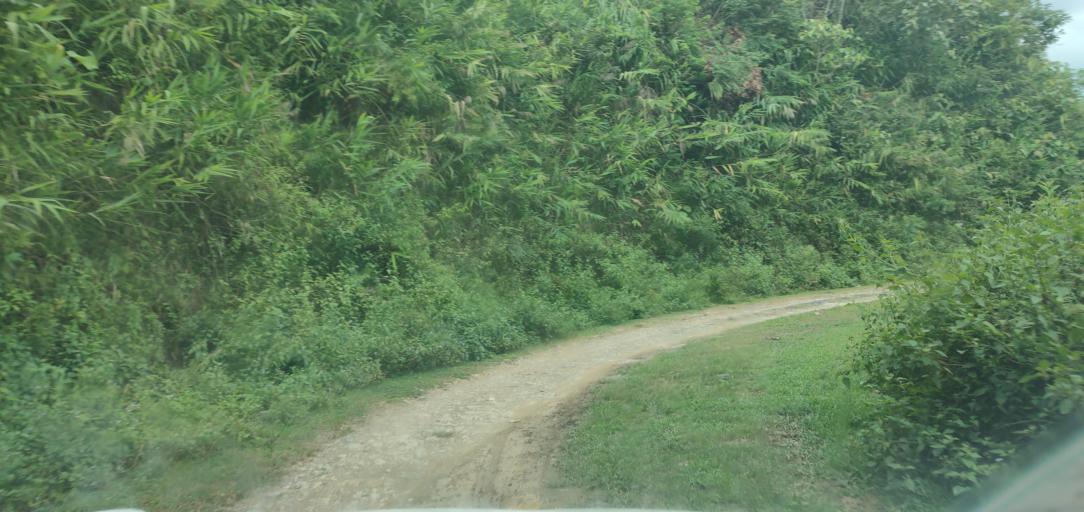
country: LA
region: Phongsali
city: Phongsali
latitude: 21.4471
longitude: 102.3105
